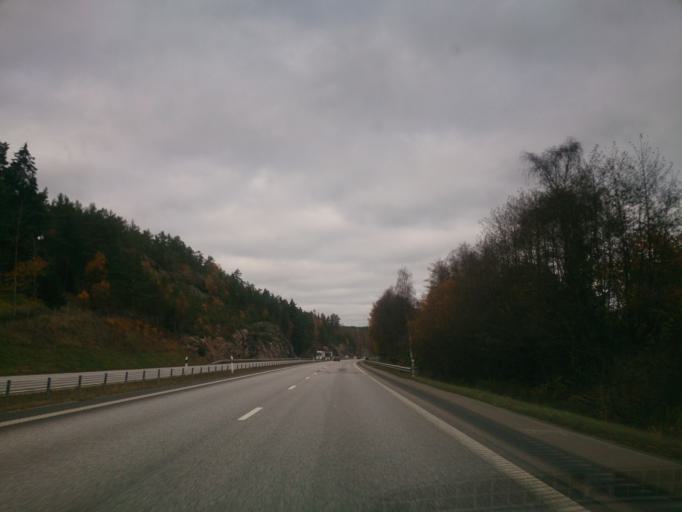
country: SE
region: OEstergoetland
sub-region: Norrkopings Kommun
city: Krokek
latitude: 58.6950
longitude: 16.3367
